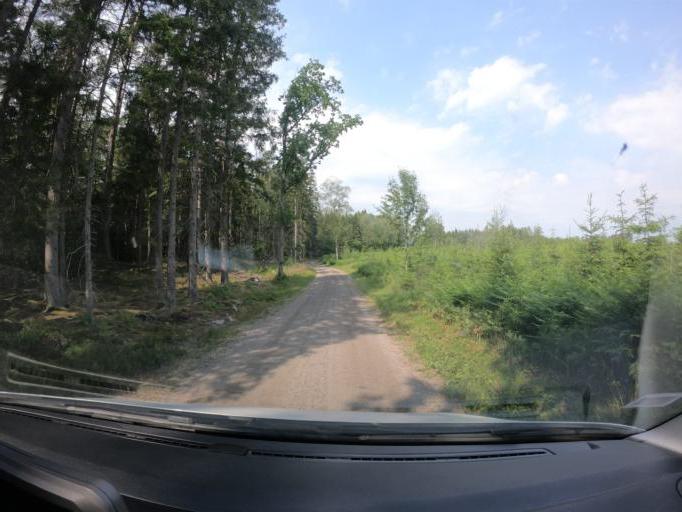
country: SE
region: Skane
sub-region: Hassleholms Kommun
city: Bjarnum
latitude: 56.2939
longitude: 13.5778
